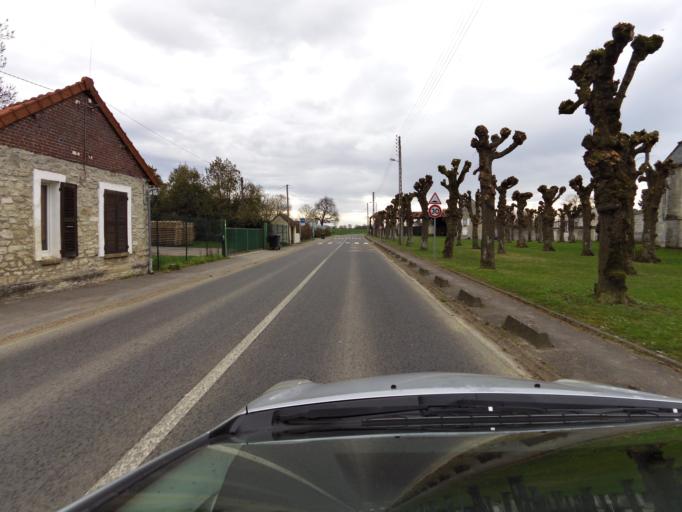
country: FR
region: Picardie
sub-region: Departement de l'Oise
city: Chamant
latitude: 49.1955
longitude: 2.6308
